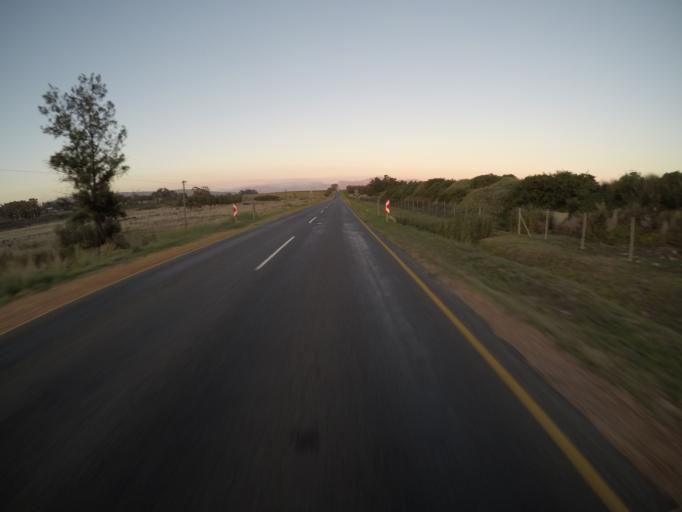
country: ZA
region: Western Cape
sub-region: Cape Winelands District Municipality
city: Paarl
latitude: -33.8066
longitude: 18.8786
